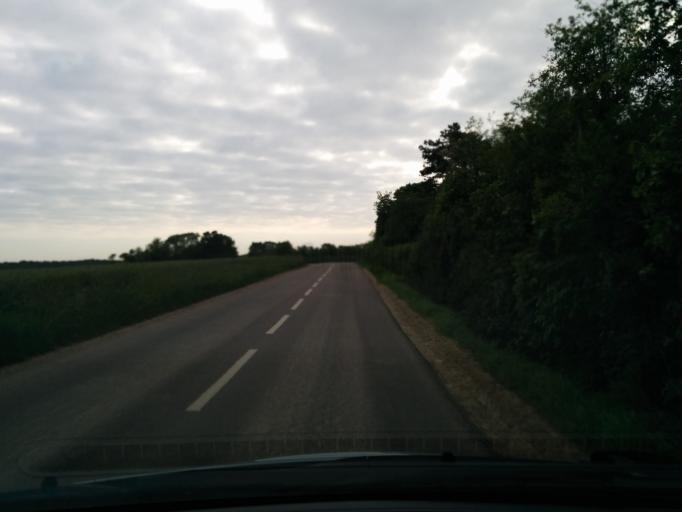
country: FR
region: Haute-Normandie
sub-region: Departement de l'Eure
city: Gasny
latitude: 49.0838
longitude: 1.6278
